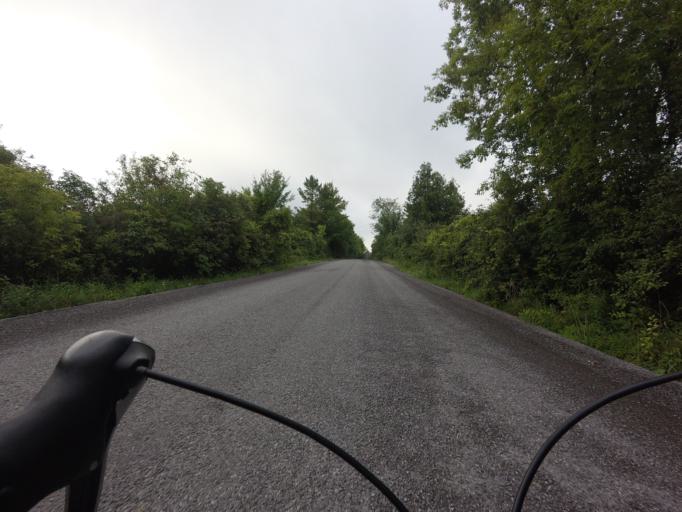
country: CA
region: Ontario
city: Bells Corners
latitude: 45.0789
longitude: -75.7572
